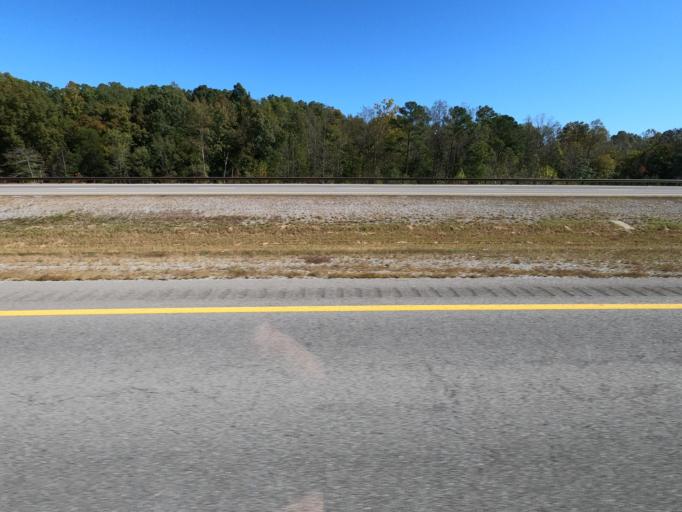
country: US
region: Tennessee
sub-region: Williamson County
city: Fairview
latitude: 35.8699
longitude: -87.0916
